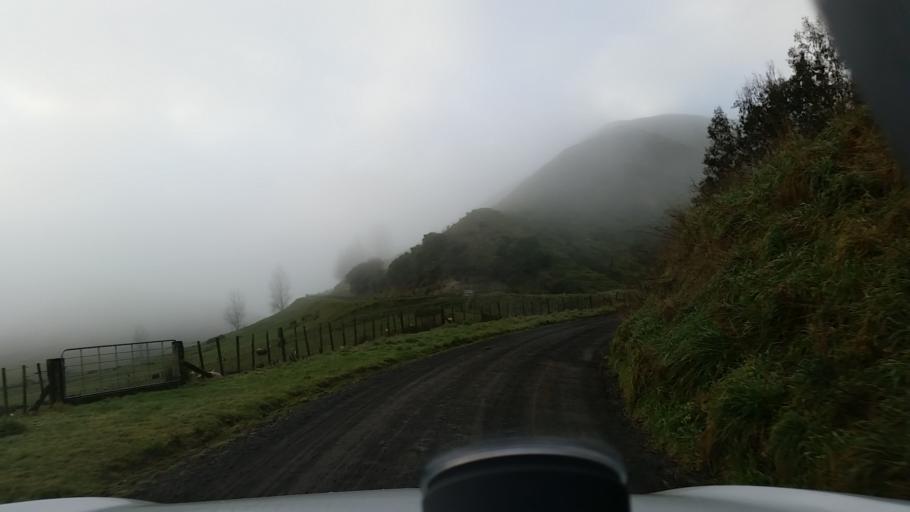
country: NZ
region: Taranaki
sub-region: South Taranaki District
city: Eltham
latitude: -39.4324
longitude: 174.4449
